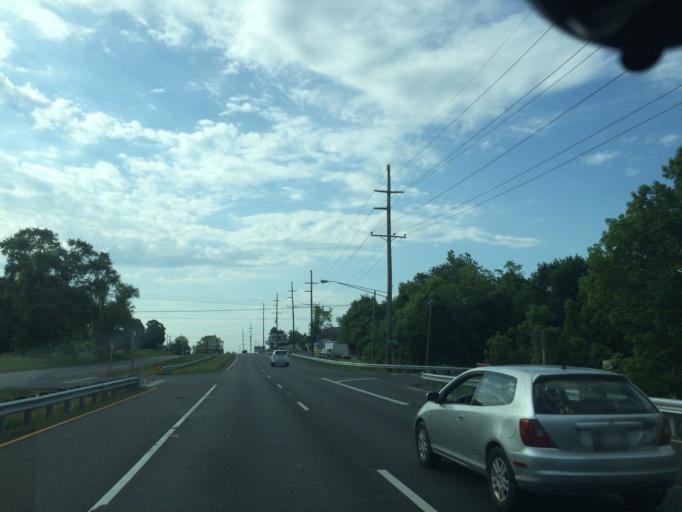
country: US
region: Maryland
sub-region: Baltimore County
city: Reisterstown
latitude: 39.5018
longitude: -76.8979
